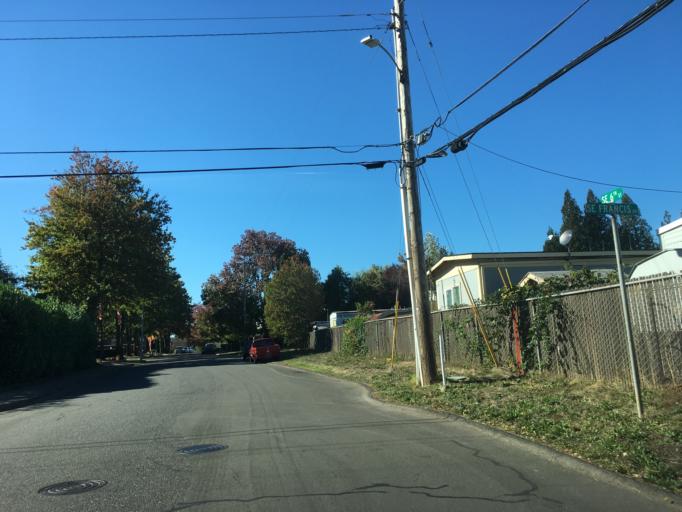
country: US
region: Oregon
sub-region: Multnomah County
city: Gresham
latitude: 45.4932
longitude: -122.4106
